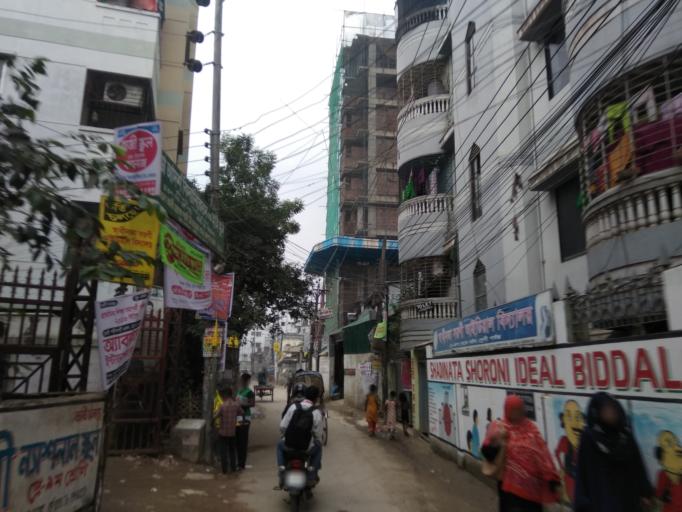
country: BD
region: Dhaka
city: Paltan
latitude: 23.7843
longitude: 90.4284
